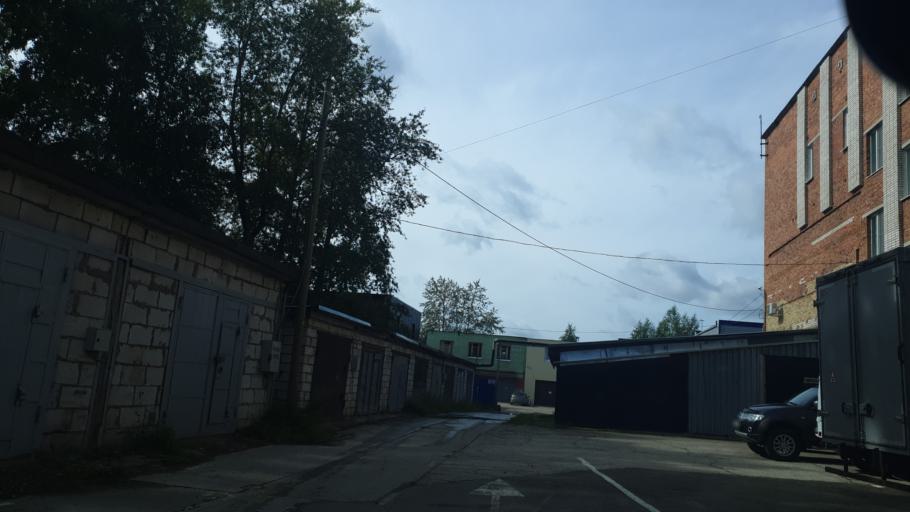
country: RU
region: Komi Republic
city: Ezhva
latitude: 61.8089
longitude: 50.7362
